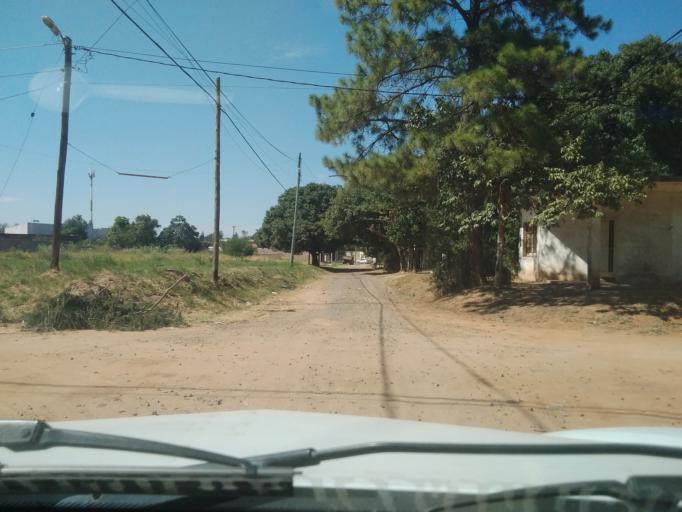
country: AR
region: Corrientes
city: Corrientes
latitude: -27.5048
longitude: -58.8092
